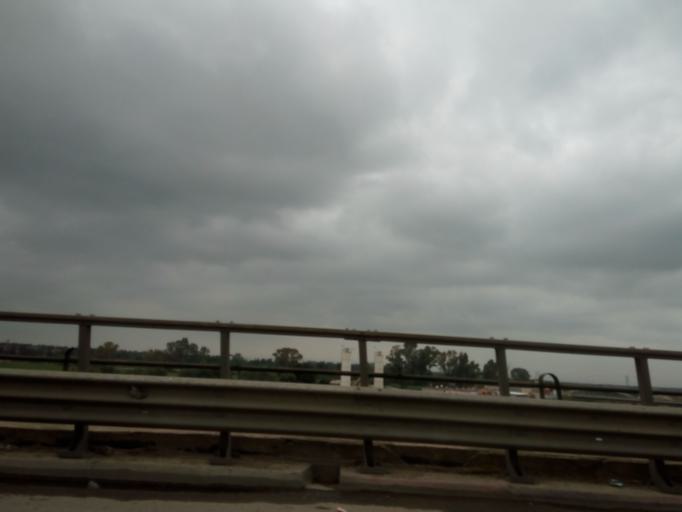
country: DZ
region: Blida
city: Chiffa
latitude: 36.4614
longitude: 2.7540
